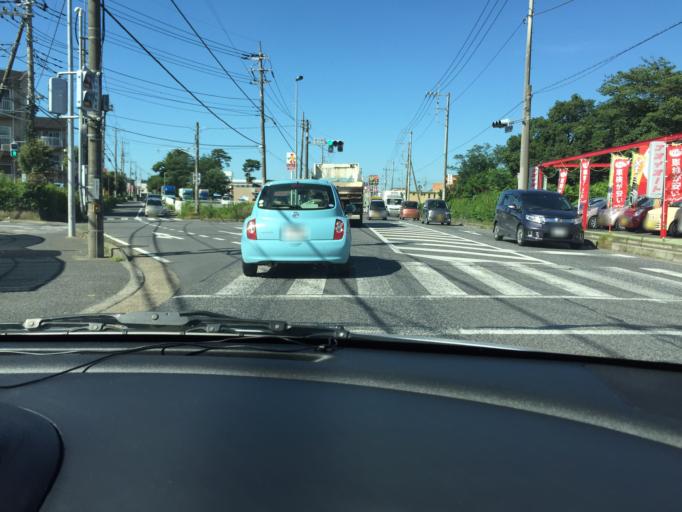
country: JP
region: Ibaraki
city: Naka
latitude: 36.0502
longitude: 140.1708
